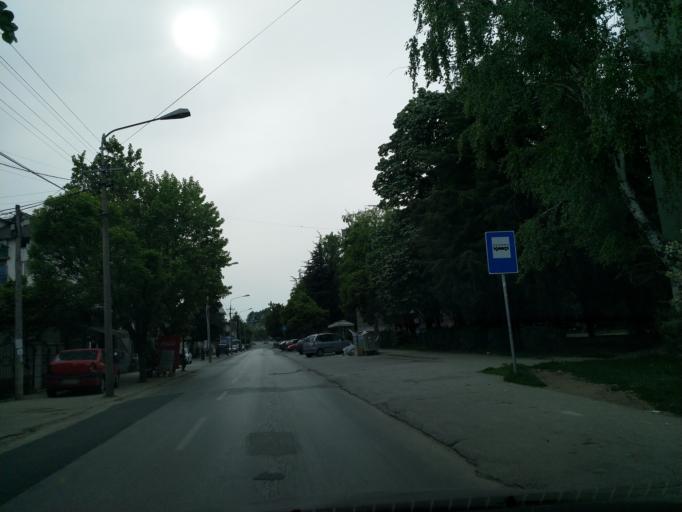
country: RS
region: Central Serbia
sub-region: Pomoravski Okrug
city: Jagodina
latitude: 43.9768
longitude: 21.2532
